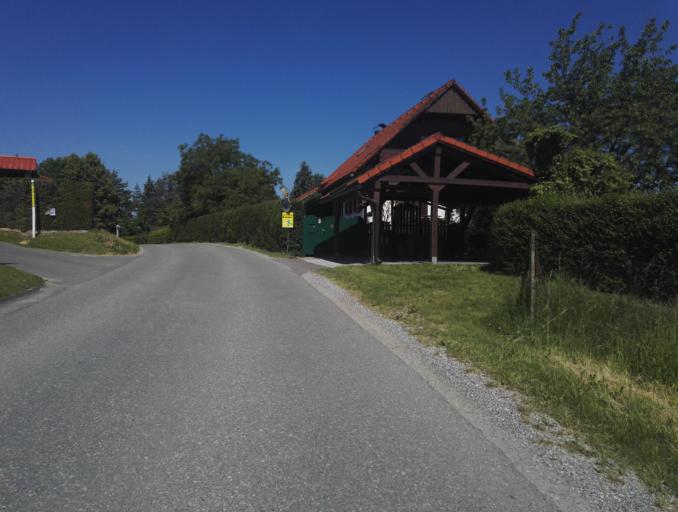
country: AT
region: Styria
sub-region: Politischer Bezirk Graz-Umgebung
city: Edelsgrub
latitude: 47.0509
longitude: 15.5671
